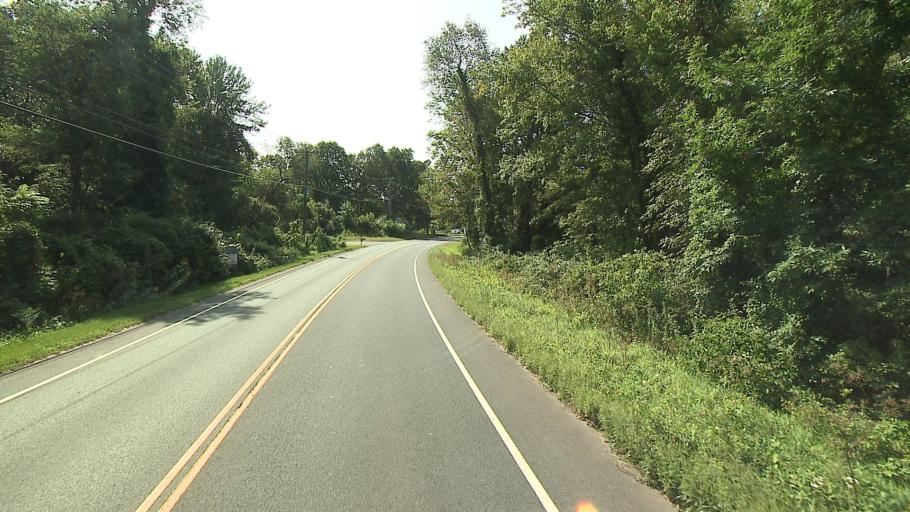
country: US
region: Connecticut
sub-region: Fairfield County
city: Newtown
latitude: 41.4316
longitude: -73.3544
